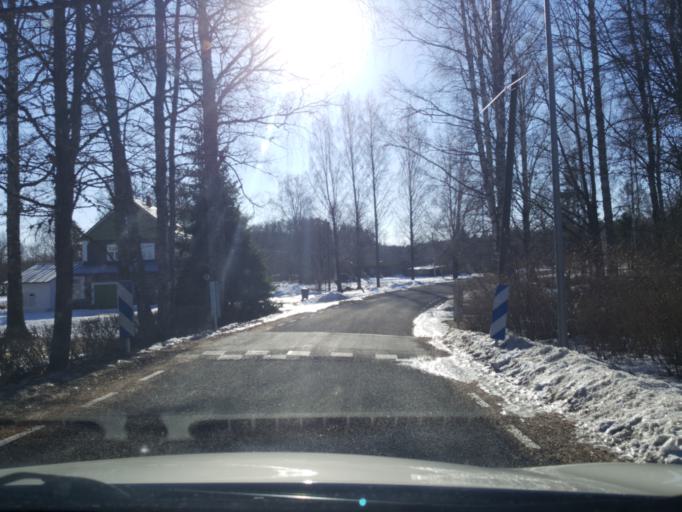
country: EE
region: Viljandimaa
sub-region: Vohma linn
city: Vohma
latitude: 58.5201
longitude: 25.6259
